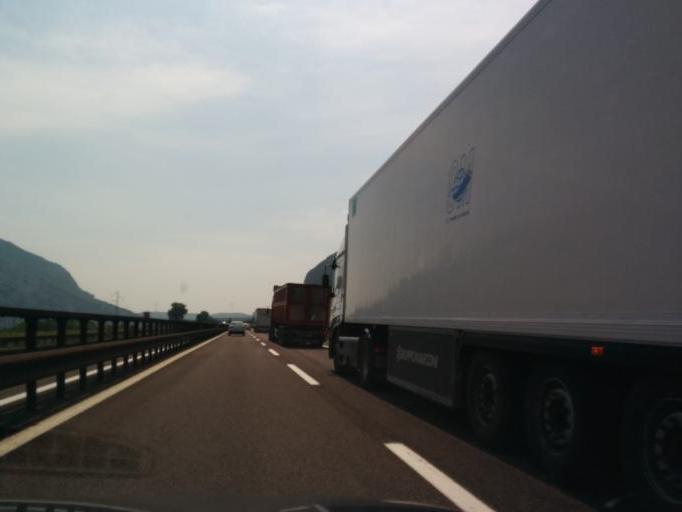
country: IT
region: Veneto
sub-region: Provincia di Verona
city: Dolce
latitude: 45.6020
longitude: 10.8451
